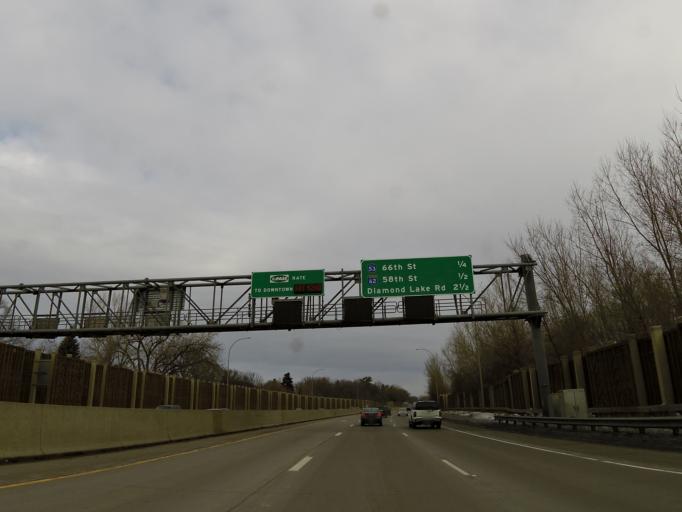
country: US
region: Minnesota
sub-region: Hennepin County
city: Richfield
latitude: 44.8760
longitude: -93.2980
